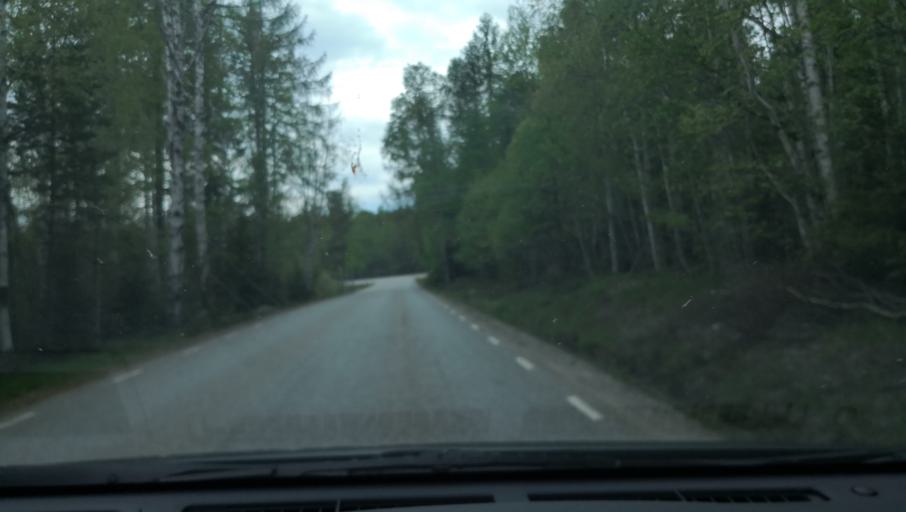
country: SE
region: Vaestmanland
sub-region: Skinnskattebergs Kommun
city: Skinnskatteberg
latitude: 59.8328
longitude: 15.5756
